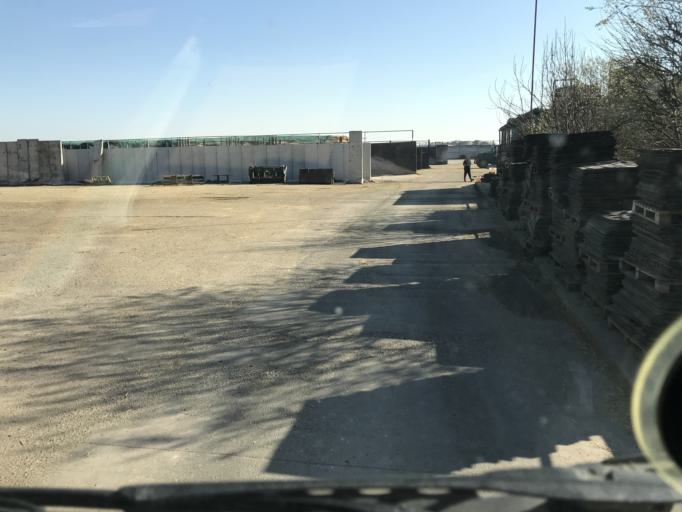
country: GB
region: England
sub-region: Cheshire West and Chester
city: Aldford
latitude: 53.1245
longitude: -2.8490
